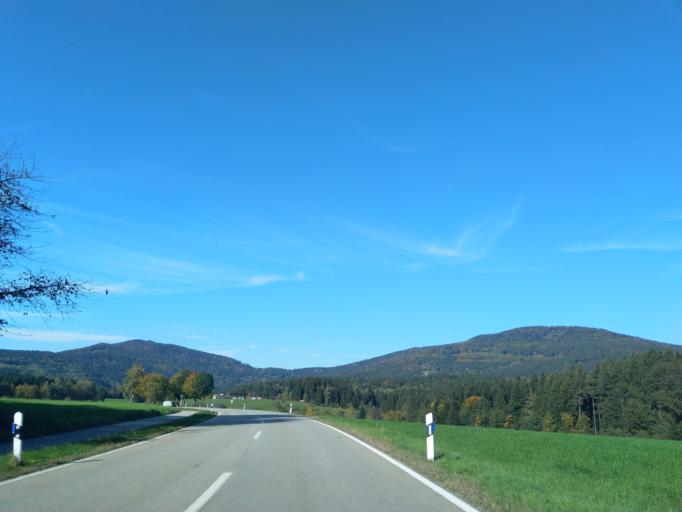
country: DE
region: Bavaria
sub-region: Lower Bavaria
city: Bernried
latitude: 48.9014
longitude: 12.9247
